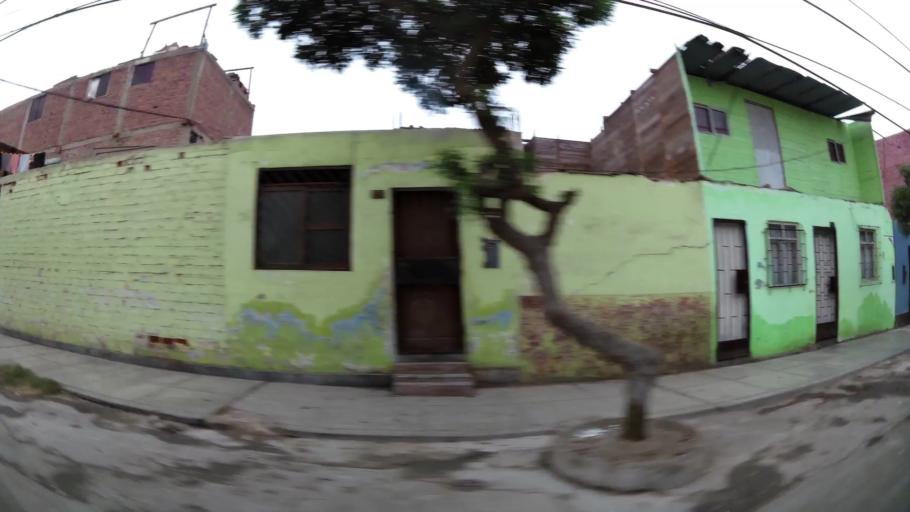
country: PE
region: Callao
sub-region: Callao
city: Callao
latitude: -12.0692
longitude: -77.1304
